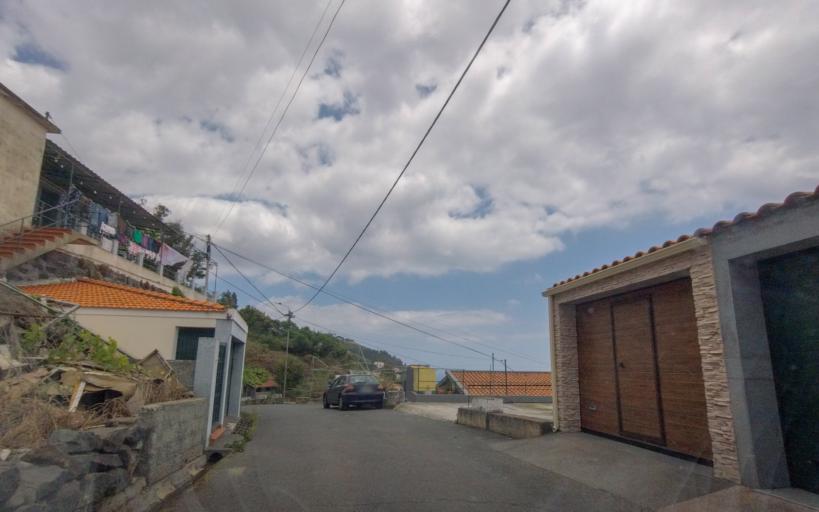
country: PT
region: Madeira
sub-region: Funchal
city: Nossa Senhora do Monte
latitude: 32.6619
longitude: -16.8821
